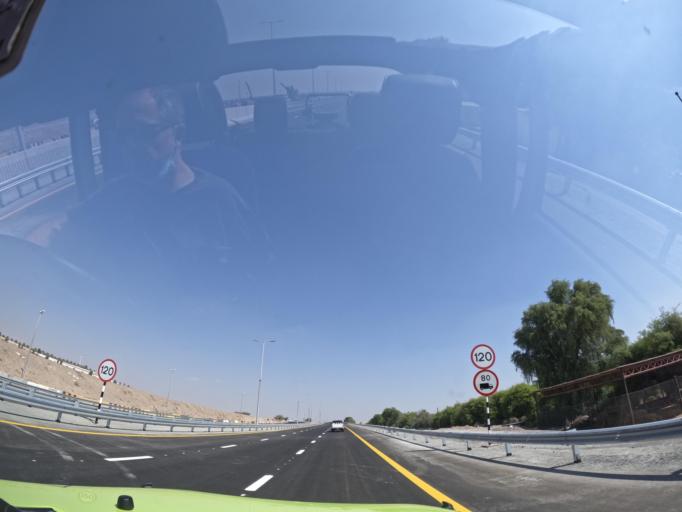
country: AE
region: Ash Shariqah
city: Adh Dhayd
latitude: 24.7770
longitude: 55.8137
